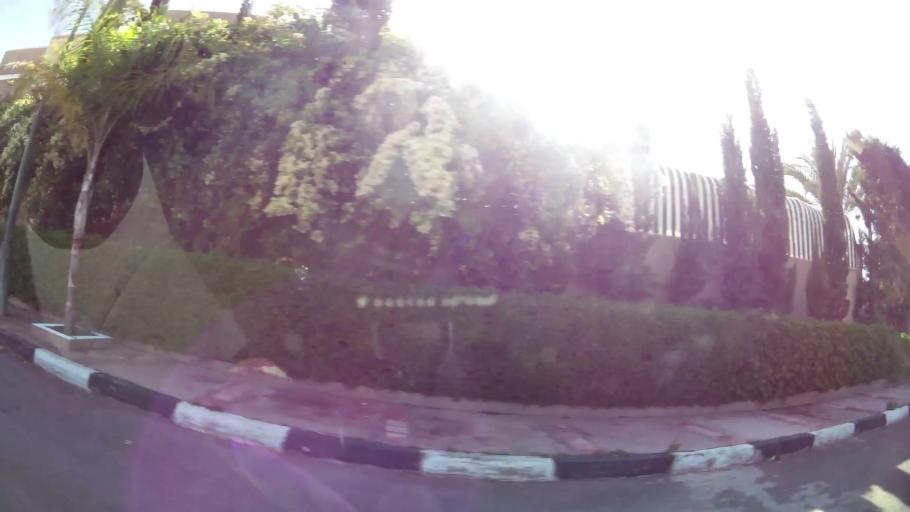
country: MA
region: Marrakech-Tensift-Al Haouz
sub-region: Marrakech
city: Marrakesh
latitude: 31.6521
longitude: -8.0511
